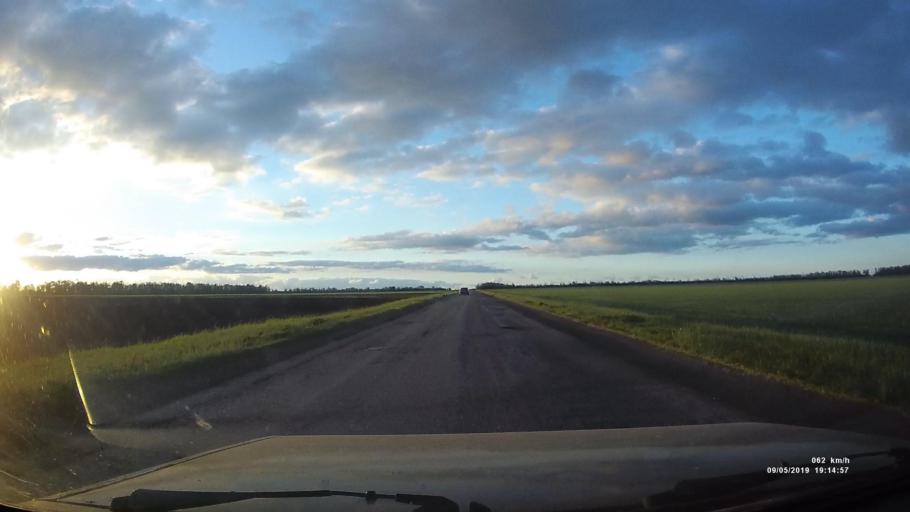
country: RU
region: Krasnodarskiy
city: Kanelovskaya
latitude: 46.7624
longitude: 39.2123
